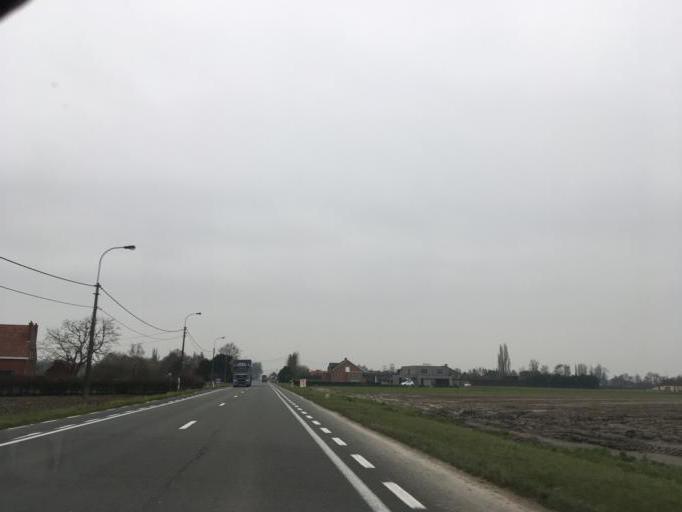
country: BE
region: Flanders
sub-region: Provincie West-Vlaanderen
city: Ingelmunster
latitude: 50.9555
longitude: 3.2458
